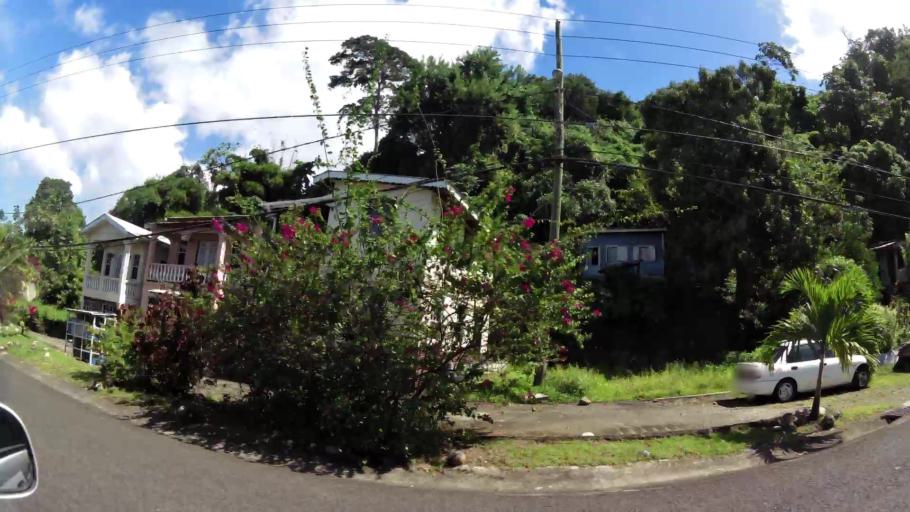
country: GD
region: Saint John
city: Gouyave
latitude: 12.1620
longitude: -61.7315
